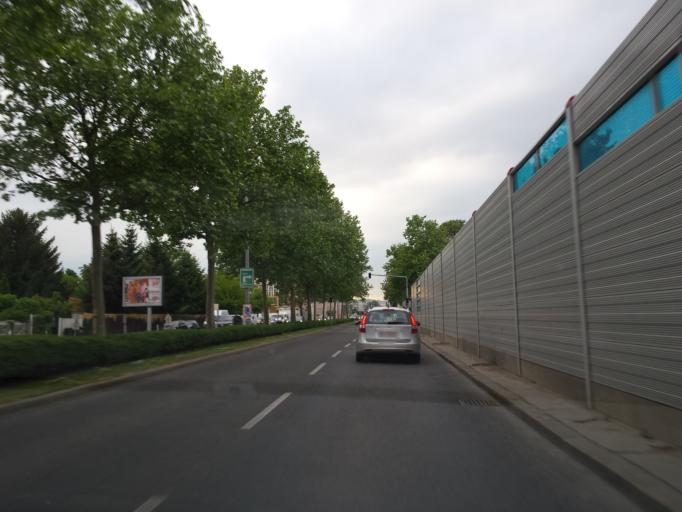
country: AT
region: Lower Austria
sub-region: Politischer Bezirk Wien-Umgebung
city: Gerasdorf bei Wien
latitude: 48.2268
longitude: 16.4615
